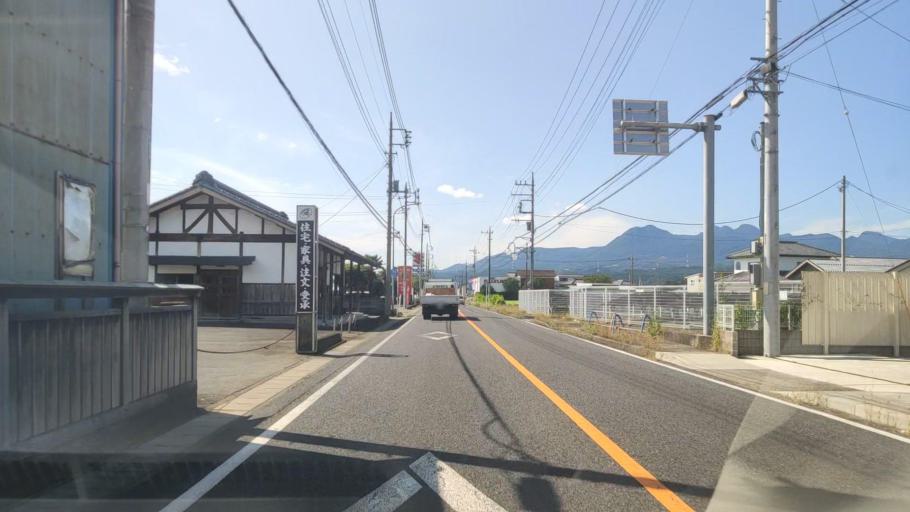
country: JP
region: Gunma
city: Shibukawa
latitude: 36.5321
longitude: 139.0172
